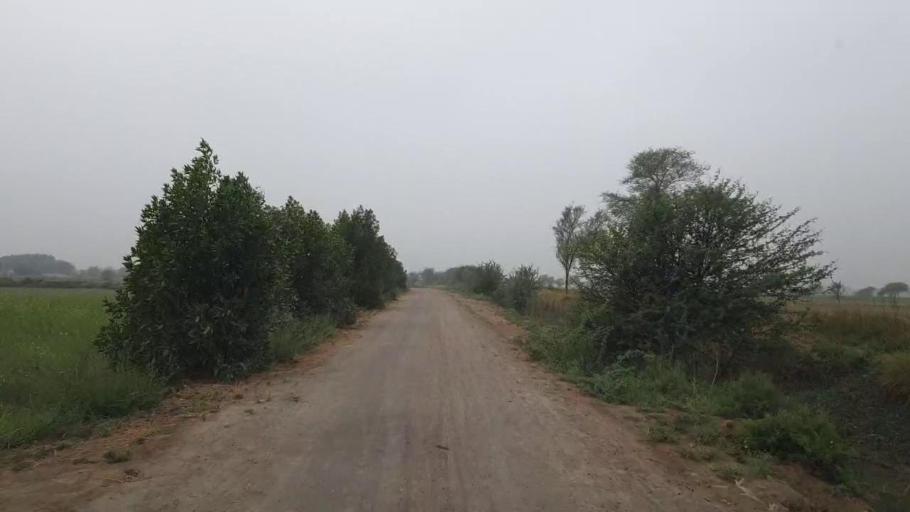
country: PK
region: Sindh
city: Badin
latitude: 24.5706
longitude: 68.6527
